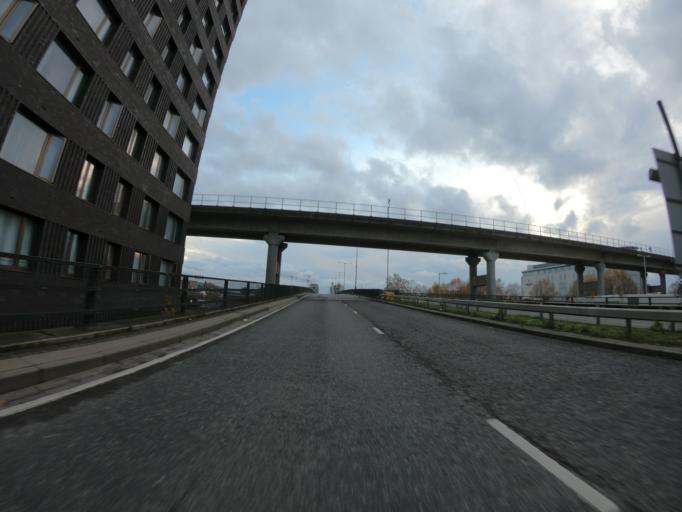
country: GB
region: England
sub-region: Greater London
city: East Ham
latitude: 51.5083
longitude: 0.0403
